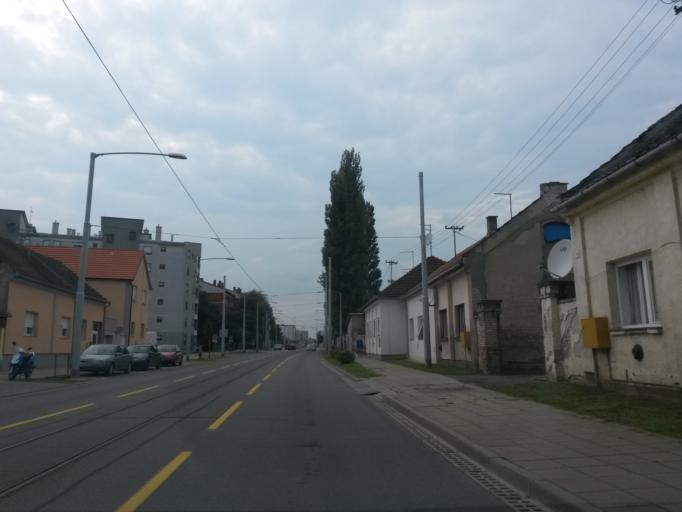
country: HR
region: Osjecko-Baranjska
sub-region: Grad Osijek
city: Osijek
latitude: 45.5471
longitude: 18.7284
